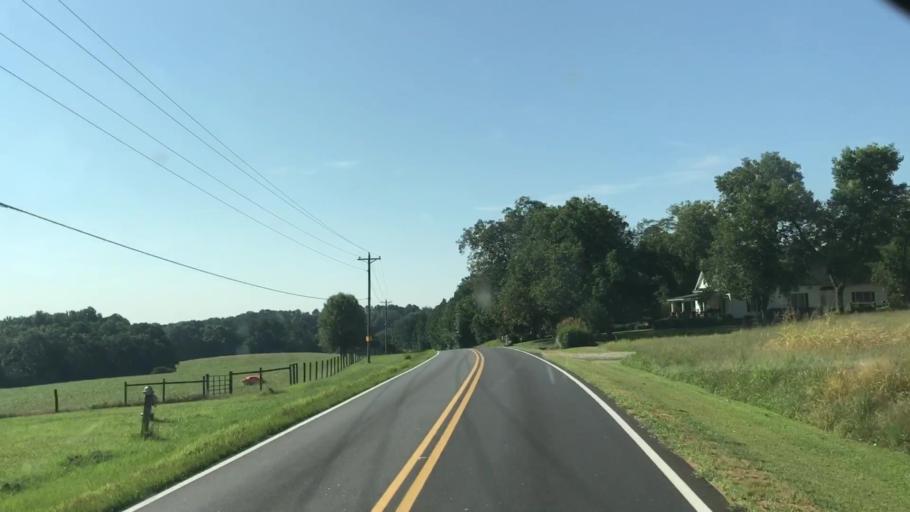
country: US
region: Georgia
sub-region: Walton County
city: Monroe
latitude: 33.8495
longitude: -83.7858
